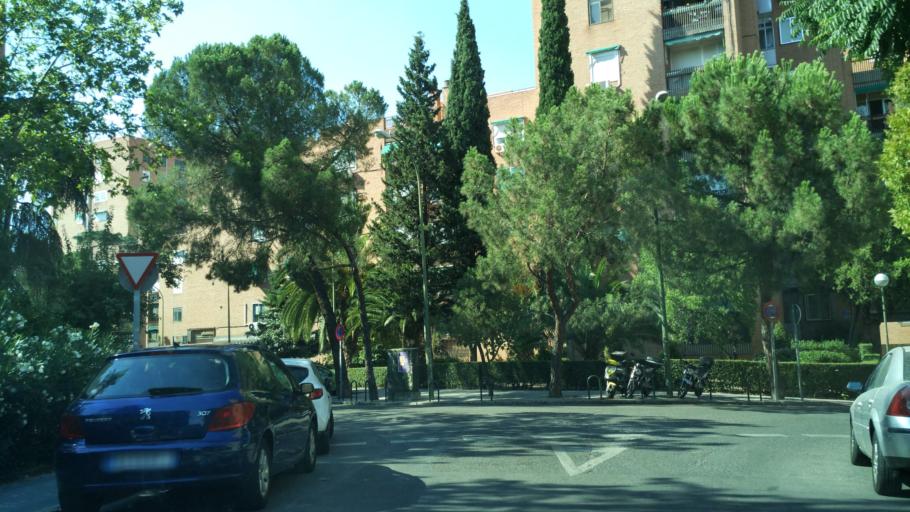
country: ES
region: Madrid
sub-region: Provincia de Madrid
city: Tetuan de las Victorias
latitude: 40.4674
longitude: -3.7217
